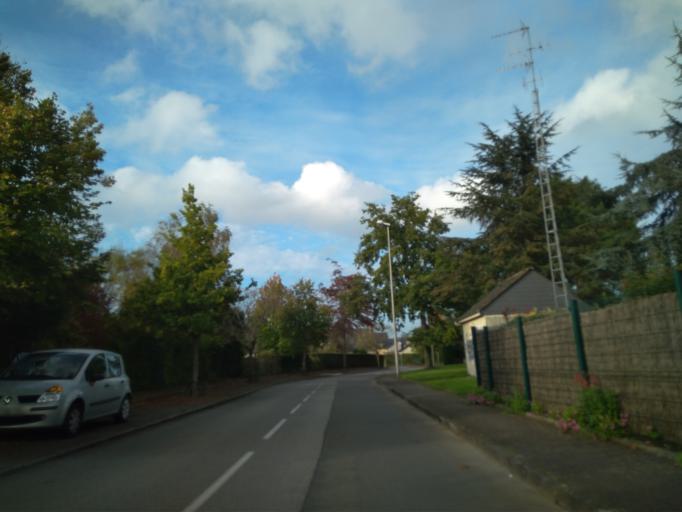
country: FR
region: Brittany
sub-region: Departement d'Ille-et-Vilaine
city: Betton
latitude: 48.1736
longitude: -1.6373
